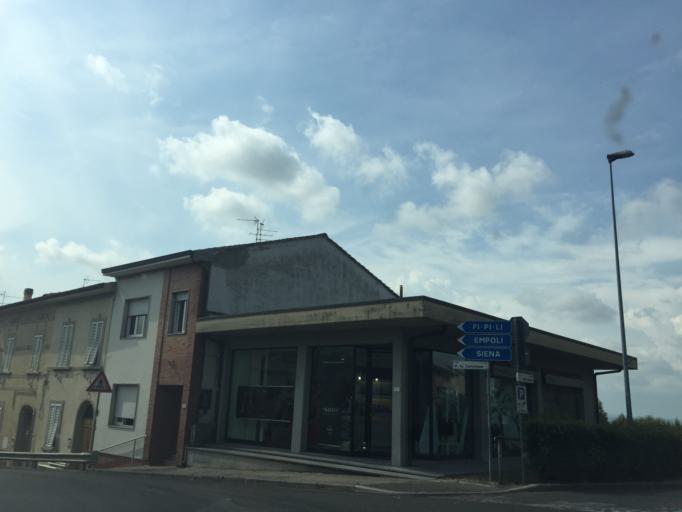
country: IT
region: Tuscany
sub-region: Province of Florence
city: Cerreto Guidi
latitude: 43.7581
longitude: 10.8812
